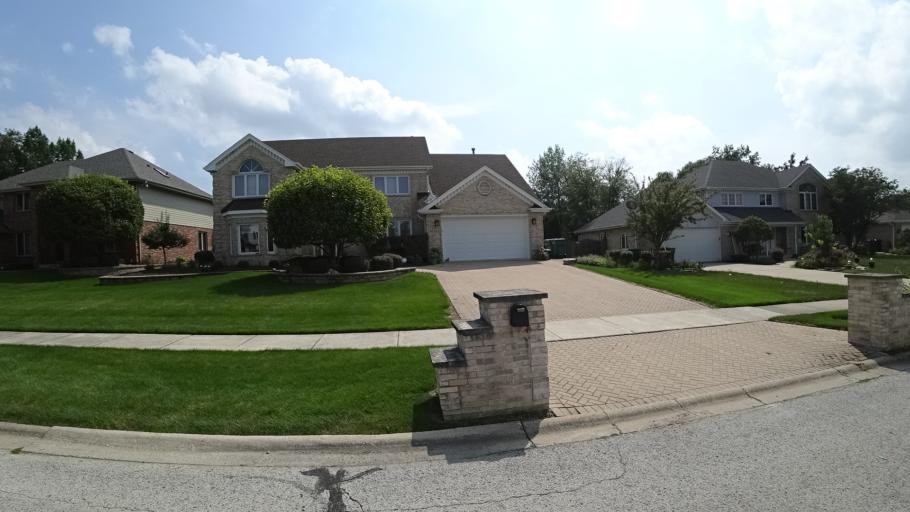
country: US
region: Illinois
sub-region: Cook County
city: Orland Park
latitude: 41.6384
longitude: -87.8913
